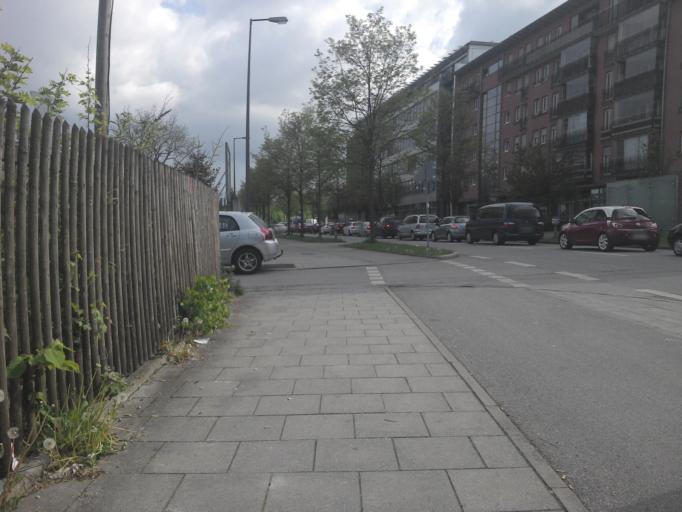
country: DE
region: Bavaria
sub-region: Upper Bavaria
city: Munich
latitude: 48.1742
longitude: 11.5285
